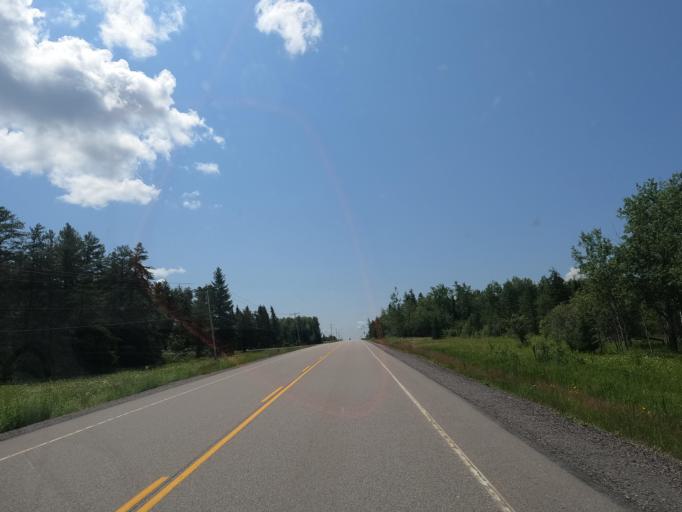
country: CA
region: Ontario
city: Dryden
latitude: 49.9109
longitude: -93.3595
